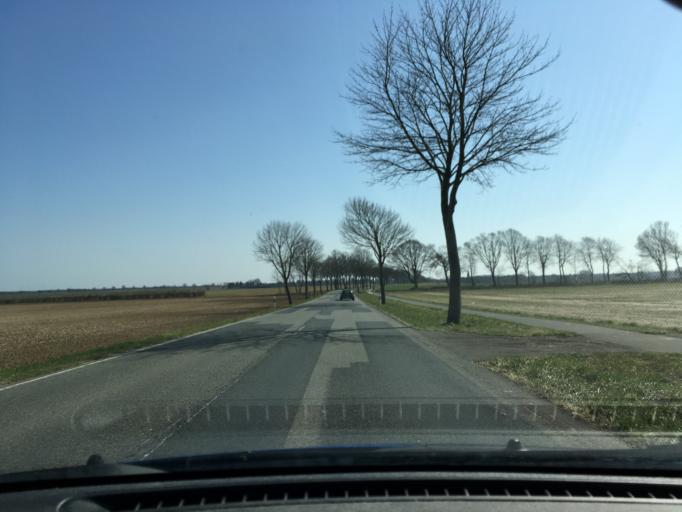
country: DE
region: Lower Saxony
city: Wriedel
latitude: 53.0465
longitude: 10.2944
